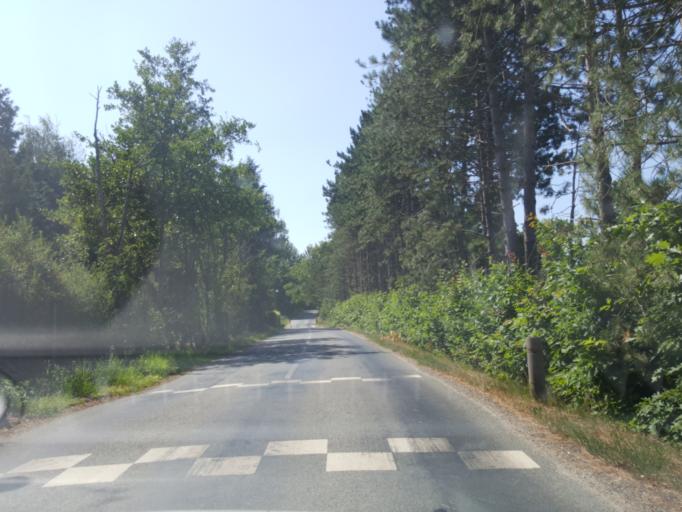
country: DK
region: Capital Region
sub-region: Fredensborg Kommune
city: Kokkedal
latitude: 55.9254
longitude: 12.4600
